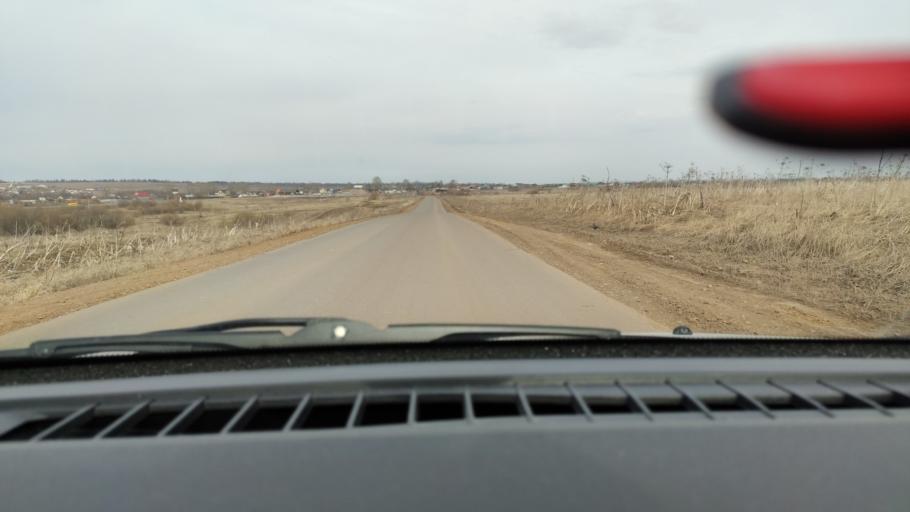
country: RU
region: Perm
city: Kultayevo
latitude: 57.9009
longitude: 55.9931
